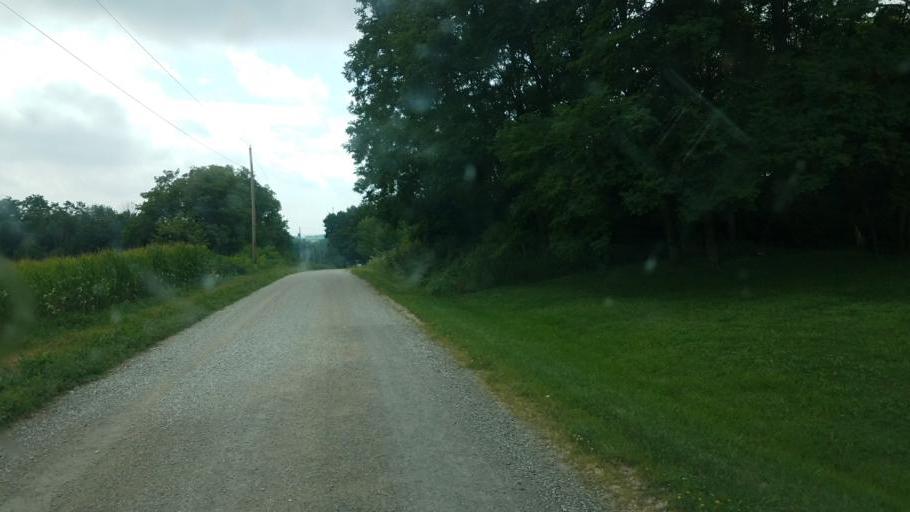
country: US
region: Ohio
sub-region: Morrow County
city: Mount Gilead
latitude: 40.5313
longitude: -82.6871
